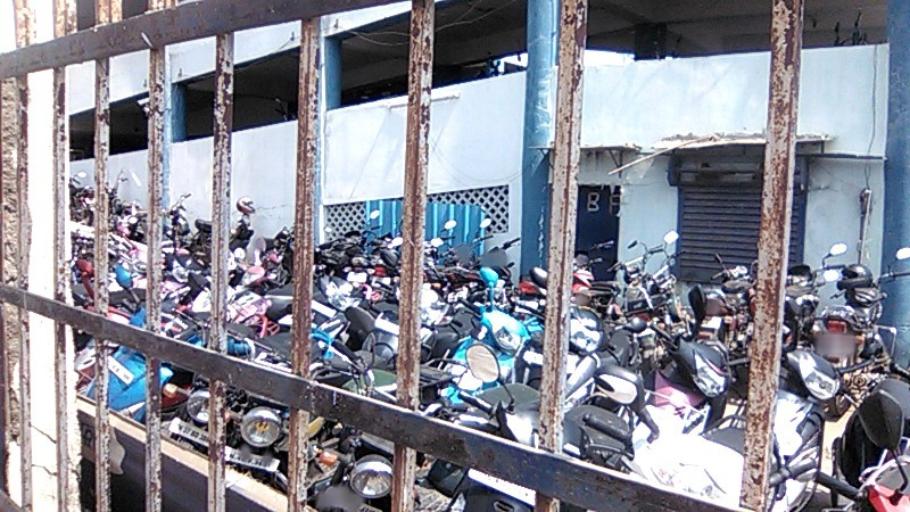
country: IN
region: Tamil Nadu
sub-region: Tiruchchirappalli
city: Tiruchirappalli
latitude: 10.7973
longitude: 78.6808
